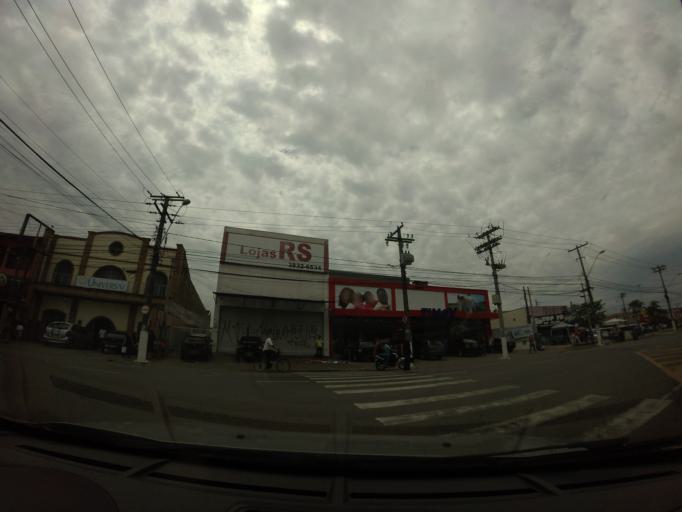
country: BR
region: Sao Paulo
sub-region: Hortolandia
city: Hortolandia
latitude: -22.8402
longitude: -47.1599
